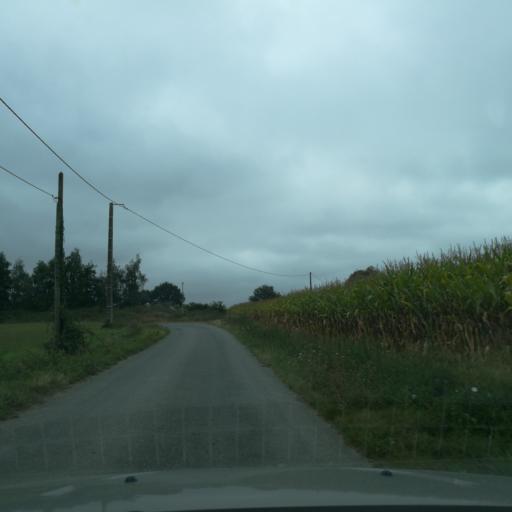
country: FR
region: Brittany
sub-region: Departement d'Ille-et-Vilaine
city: Montauban-de-Bretagne
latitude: 48.1851
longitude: -2.0035
